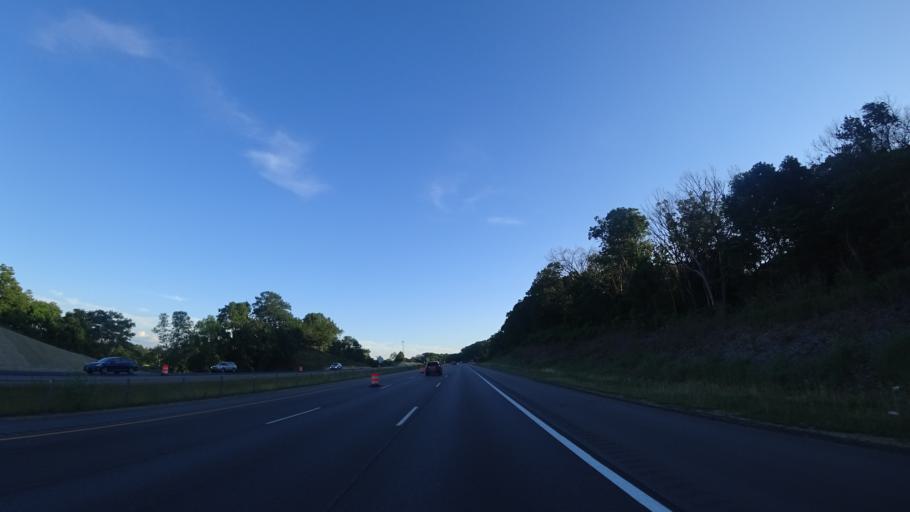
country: US
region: Michigan
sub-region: Berrien County
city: Bridgman
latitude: 41.9417
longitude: -86.5681
